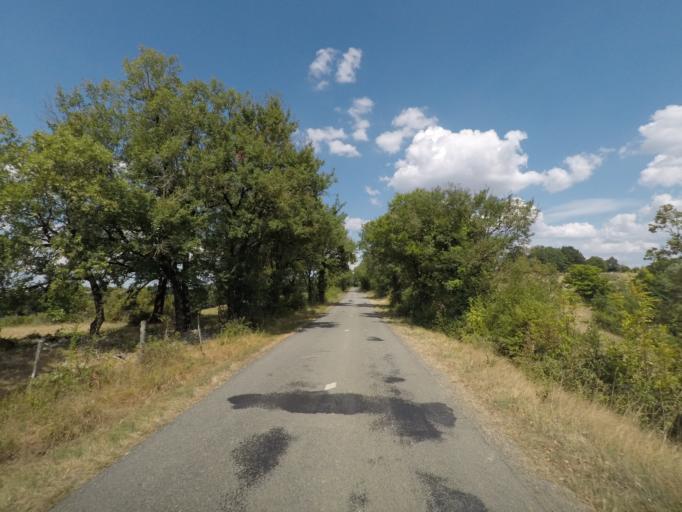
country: FR
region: Midi-Pyrenees
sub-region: Departement du Lot
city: Le Vigan
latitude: 44.6143
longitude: 1.5928
